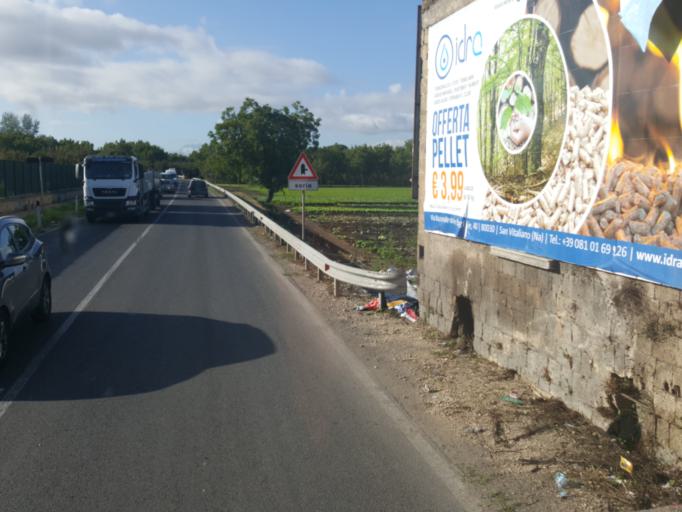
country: IT
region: Campania
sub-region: Provincia di Napoli
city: Nola
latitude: 40.9270
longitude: 14.5105
